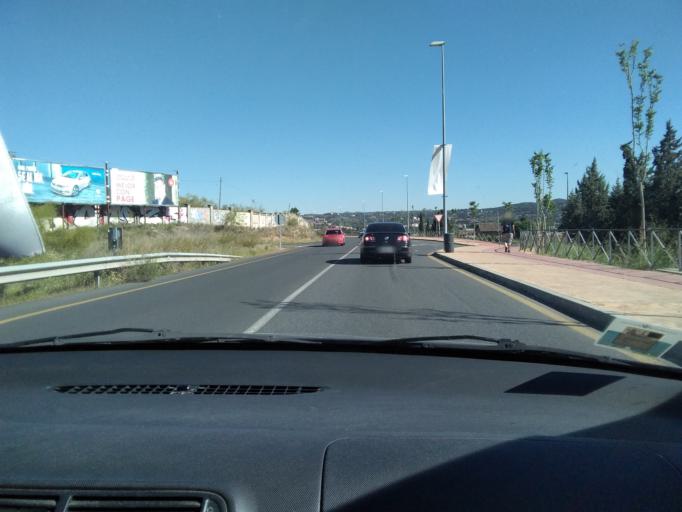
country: ES
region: Castille-La Mancha
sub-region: Province of Toledo
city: Toledo
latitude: 39.8831
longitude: -4.0529
